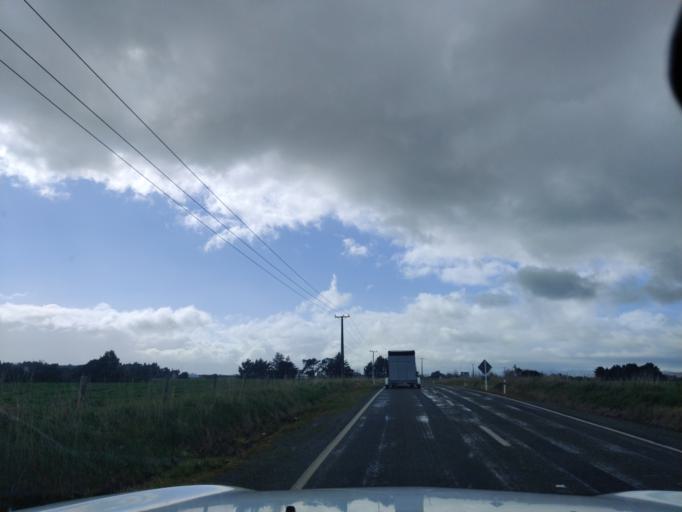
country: NZ
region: Manawatu-Wanganui
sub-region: Palmerston North City
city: Palmerston North
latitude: -40.4306
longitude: 175.5611
